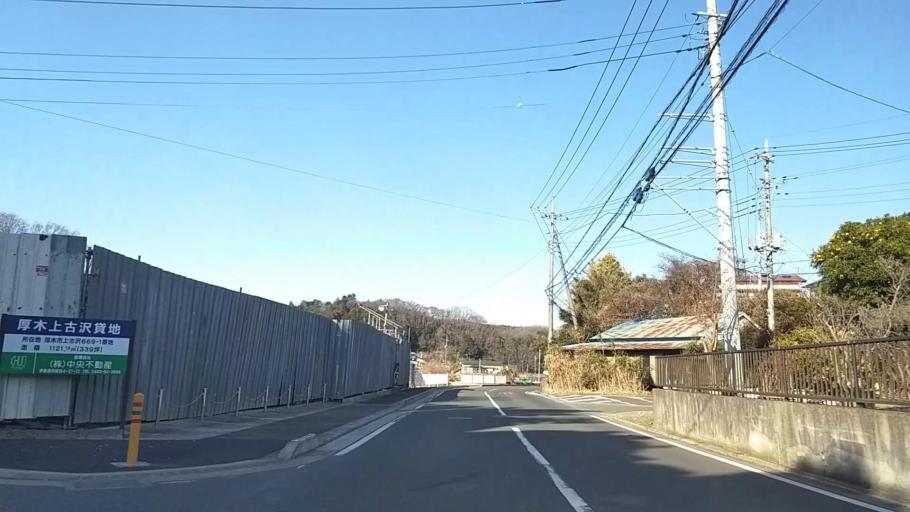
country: JP
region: Kanagawa
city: Atsugi
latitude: 35.4563
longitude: 139.3124
